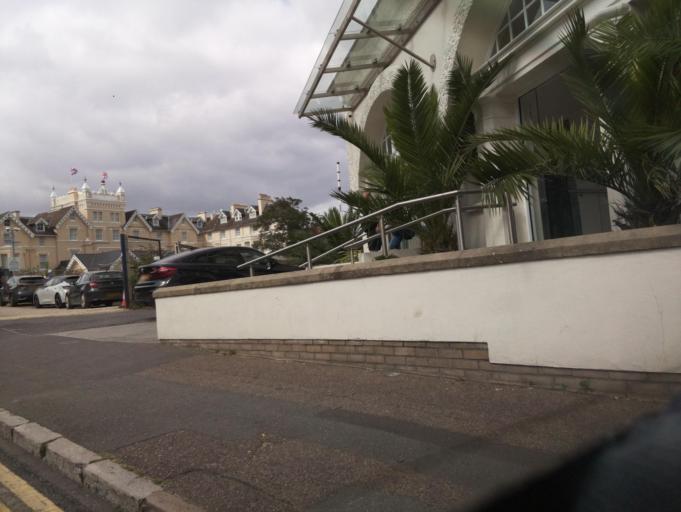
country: GB
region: England
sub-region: Bournemouth
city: Bournemouth
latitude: 50.7171
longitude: -1.8780
